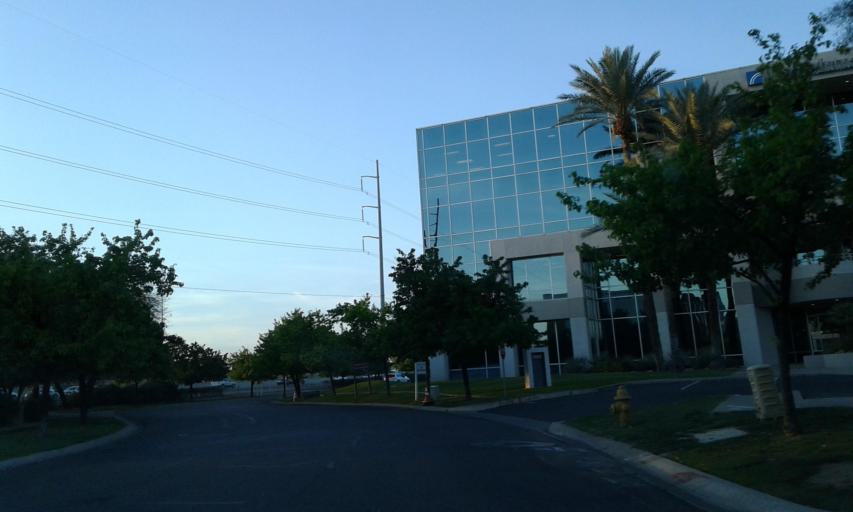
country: US
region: Arizona
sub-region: Maricopa County
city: Glendale
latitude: 33.5856
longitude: -112.1159
